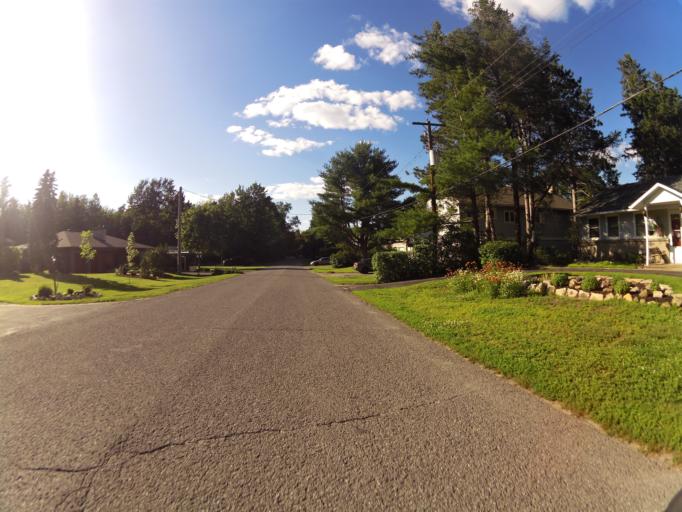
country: CA
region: Ontario
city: Bells Corners
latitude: 45.3212
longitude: -75.7417
